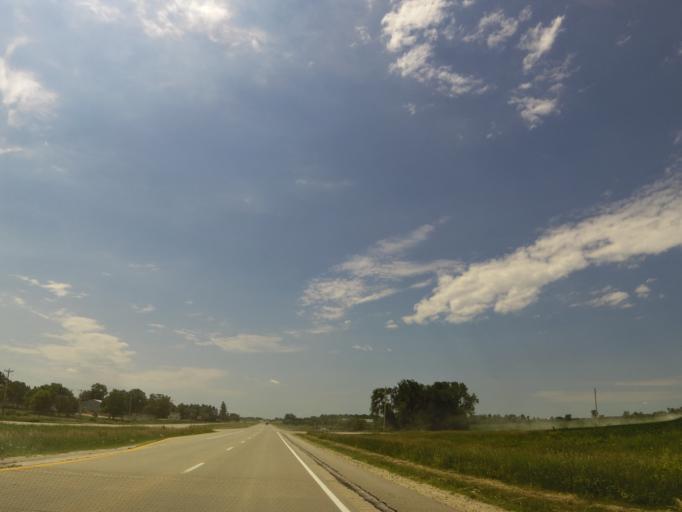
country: US
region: Iowa
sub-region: Bremer County
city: Denver
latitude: 42.7312
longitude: -92.3377
